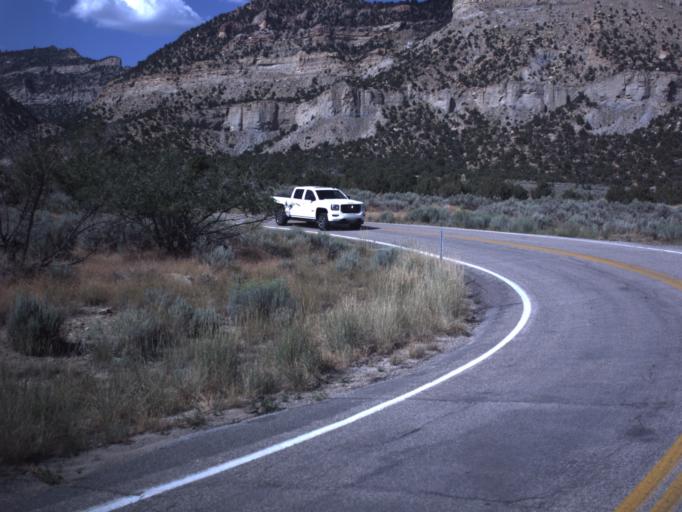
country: US
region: Utah
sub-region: Carbon County
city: Helper
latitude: 39.6843
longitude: -110.8033
